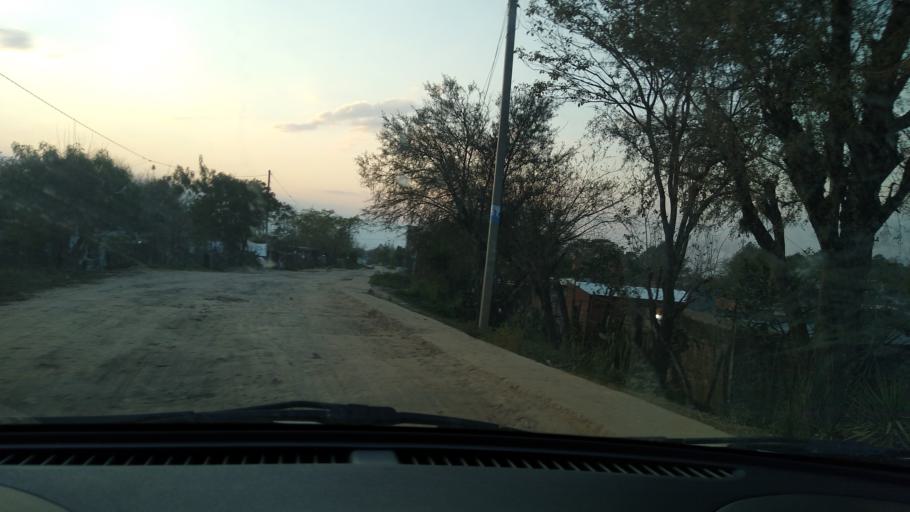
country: AR
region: Chaco
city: Barranqueras
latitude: -27.4625
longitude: -58.9536
